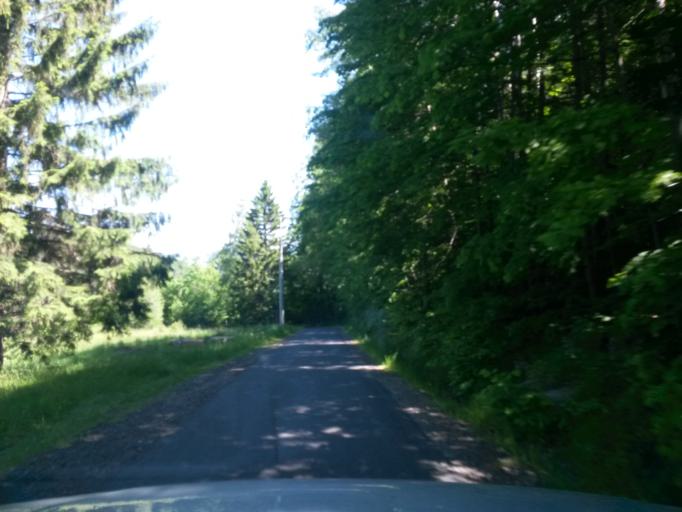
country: PL
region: Lower Silesian Voivodeship
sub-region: Powiat jeleniogorski
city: Podgorzyn
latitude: 50.8166
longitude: 15.6563
